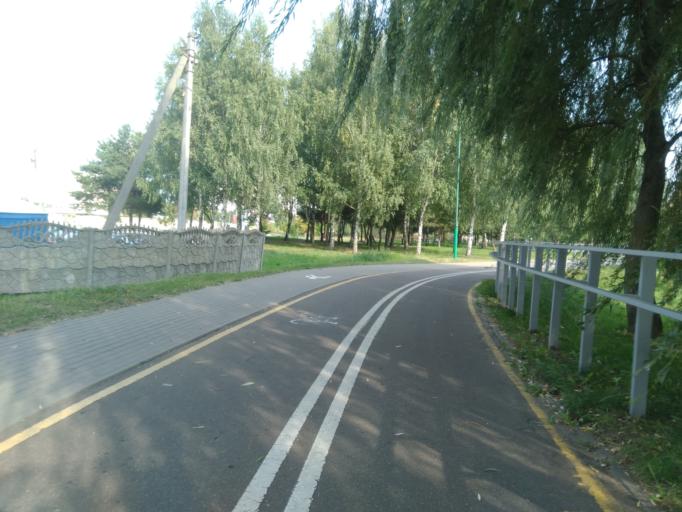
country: BY
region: Minsk
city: Minsk
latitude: 53.8707
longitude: 27.5867
